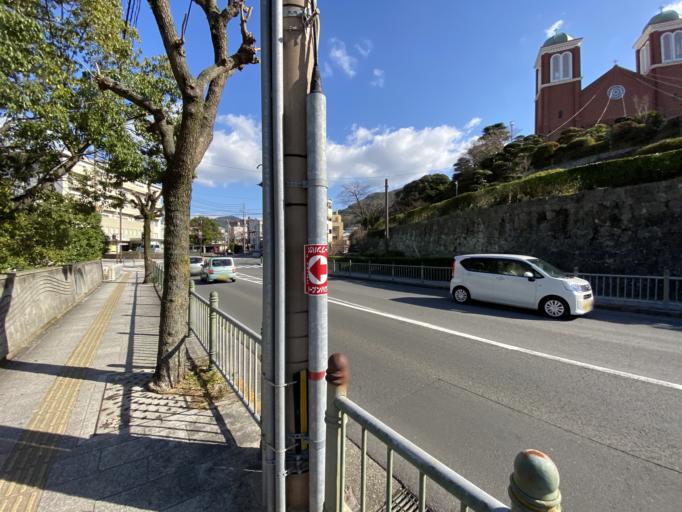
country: JP
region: Nagasaki
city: Nagasaki-shi
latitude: 32.7765
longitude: 129.8675
